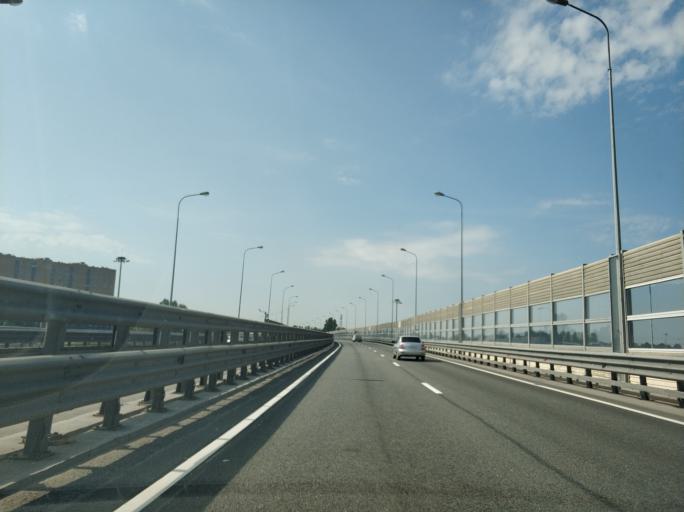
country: RU
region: St.-Petersburg
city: Krasnogvargeisky
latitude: 59.9826
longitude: 30.5113
